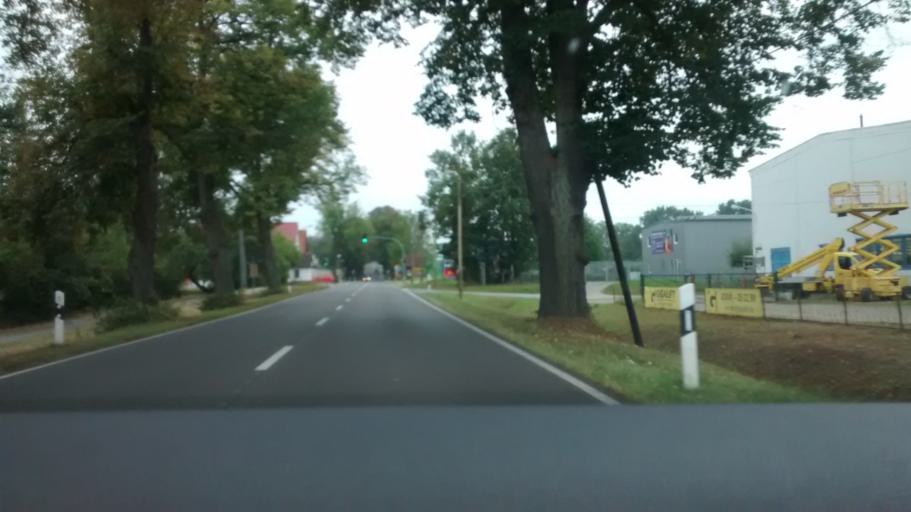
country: DE
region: Mecklenburg-Vorpommern
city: Wismar
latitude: 53.8665
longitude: 11.4509
